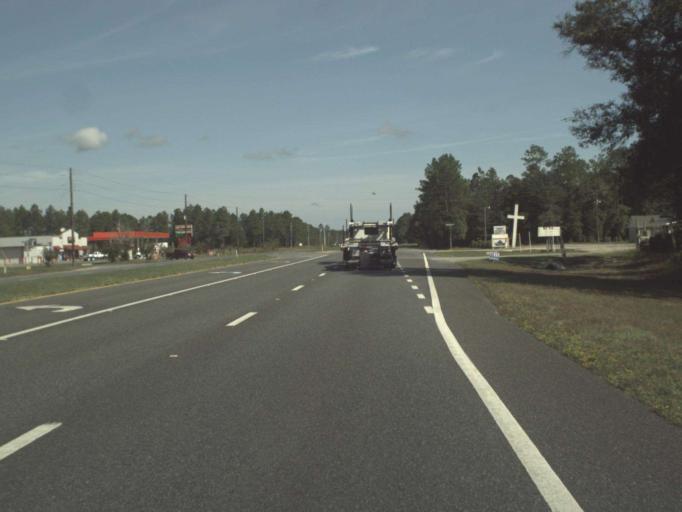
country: US
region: Florida
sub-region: Bay County
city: Youngstown
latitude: 30.4895
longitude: -85.4173
